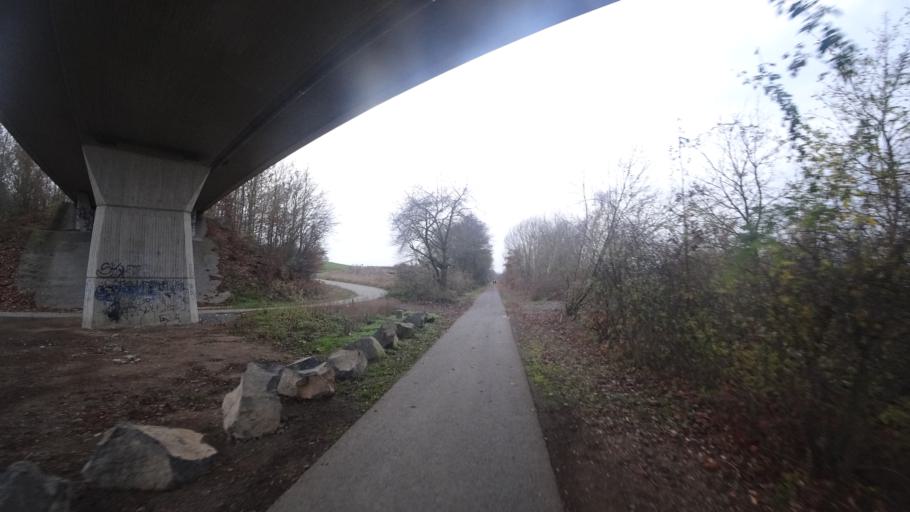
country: DE
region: Rheinland-Pfalz
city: Ochtendung
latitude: 50.3499
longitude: 7.4096
